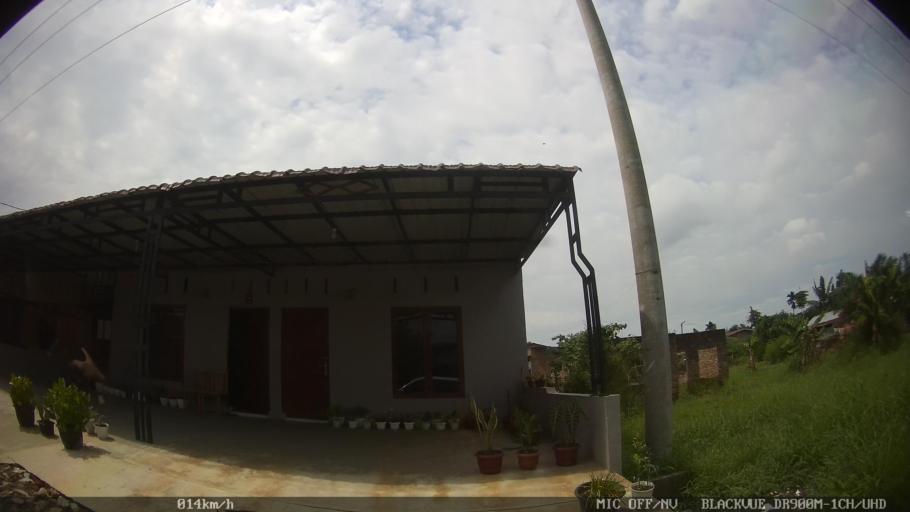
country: ID
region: North Sumatra
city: Sunggal
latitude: 3.6237
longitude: 98.6040
